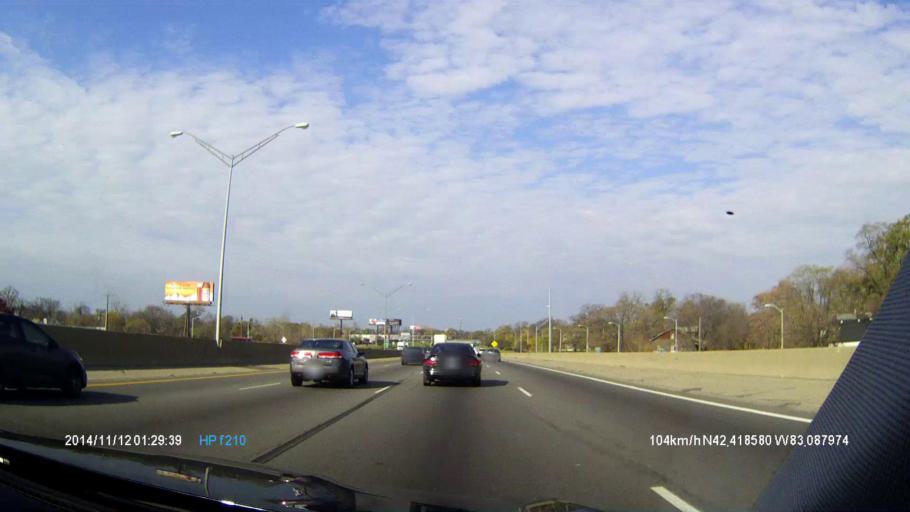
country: US
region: Michigan
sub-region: Wayne County
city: Highland Park
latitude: 42.4187
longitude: -83.0874
